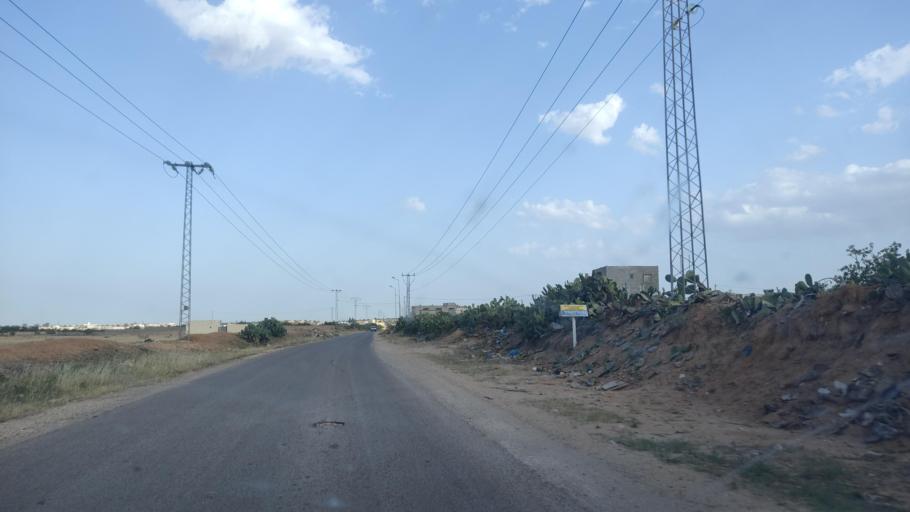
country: TN
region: Safaqis
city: Sfax
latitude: 34.8513
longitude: 10.6108
